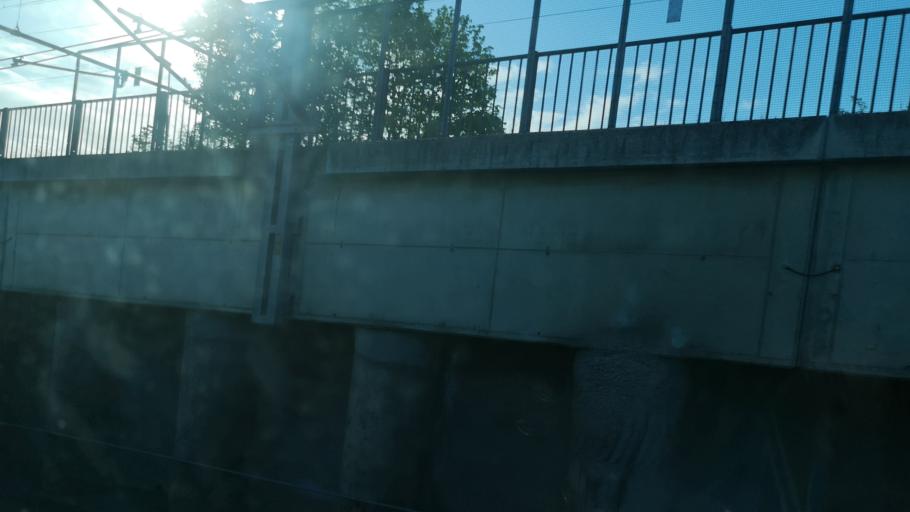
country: AT
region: Lower Austria
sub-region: Politischer Bezirk Wien-Umgebung
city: Schwechat
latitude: 48.1411
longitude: 16.4576
